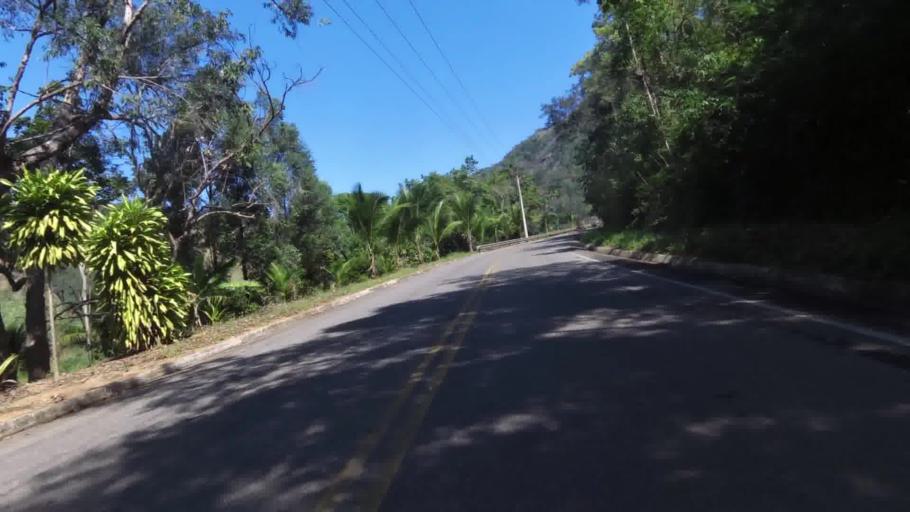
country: BR
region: Espirito Santo
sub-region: Alfredo Chaves
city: Alfredo Chaves
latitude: -20.6154
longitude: -40.7803
